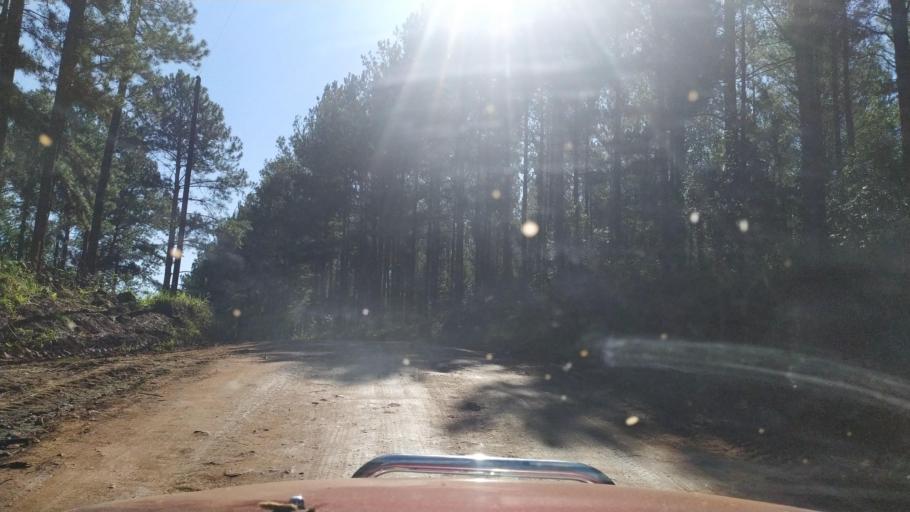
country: AR
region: Misiones
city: El Alcazar
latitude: -26.7274
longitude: -54.6801
